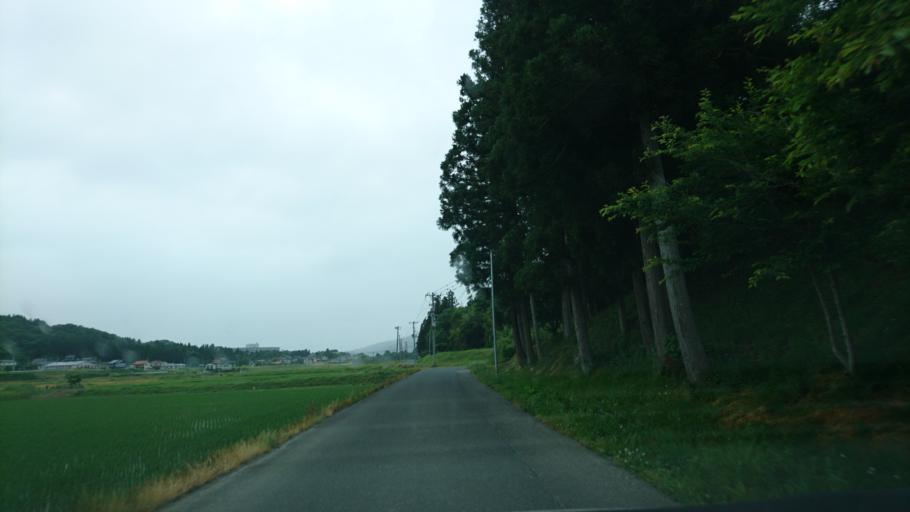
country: JP
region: Iwate
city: Ichinoseki
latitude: 38.9247
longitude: 141.1762
